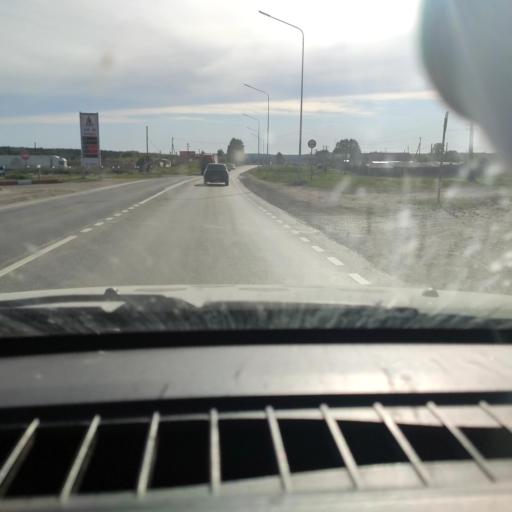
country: RU
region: Kirov
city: Vakhrushi
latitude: 58.6773
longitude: 50.0187
